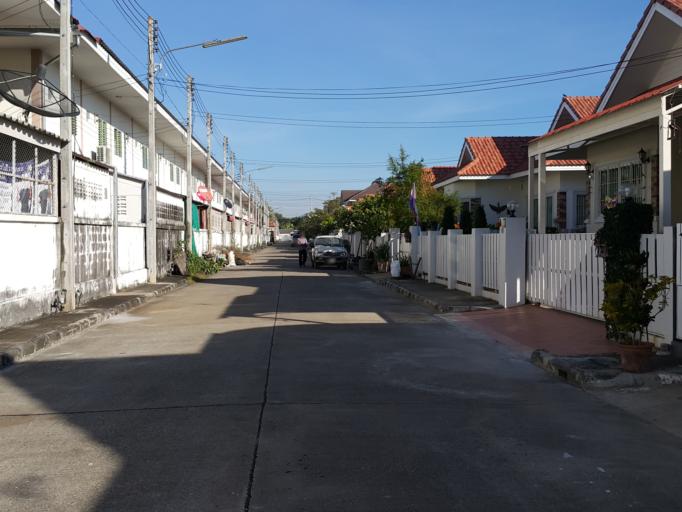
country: TH
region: Chiang Mai
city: San Kamphaeng
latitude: 18.7753
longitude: 99.0833
